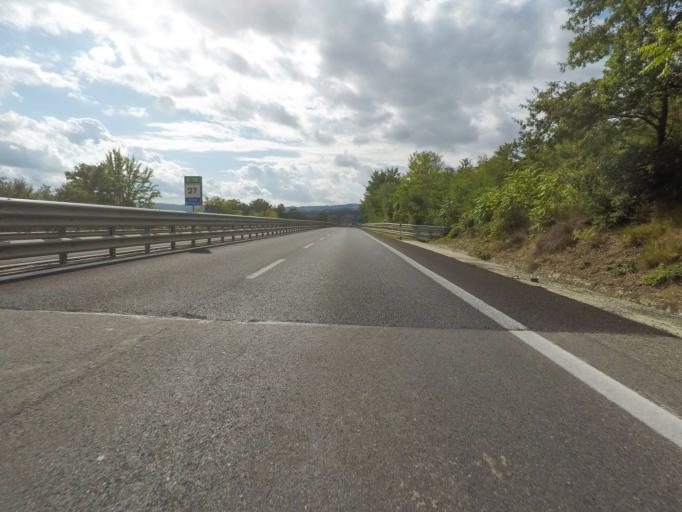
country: IT
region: Tuscany
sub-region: Provincia di Siena
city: Serre di Rapolano
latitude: 43.2758
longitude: 11.6293
